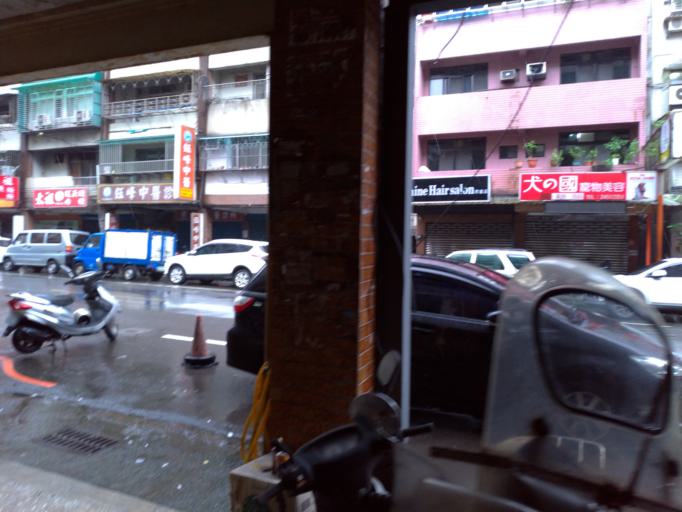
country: TW
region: Taiwan
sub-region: Keelung
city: Keelung
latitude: 25.0819
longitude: 121.6971
